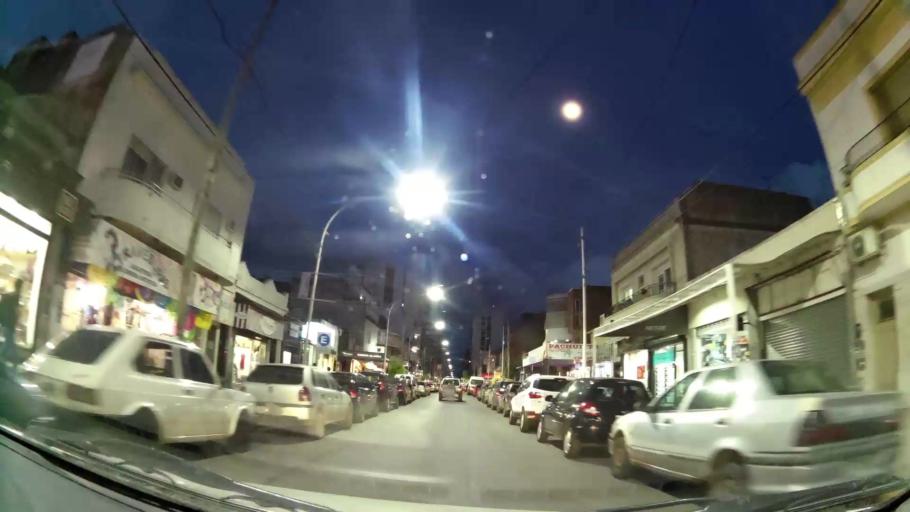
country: AR
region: Buenos Aires
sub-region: Partido de Quilmes
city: Quilmes
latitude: -34.7021
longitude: -58.3152
